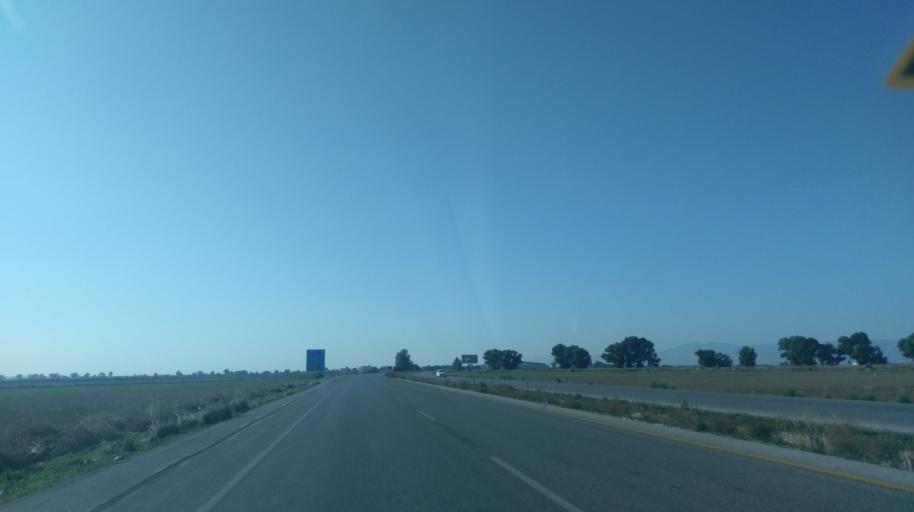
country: CY
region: Ammochostos
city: Lefkonoiko
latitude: 35.1715
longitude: 33.7793
